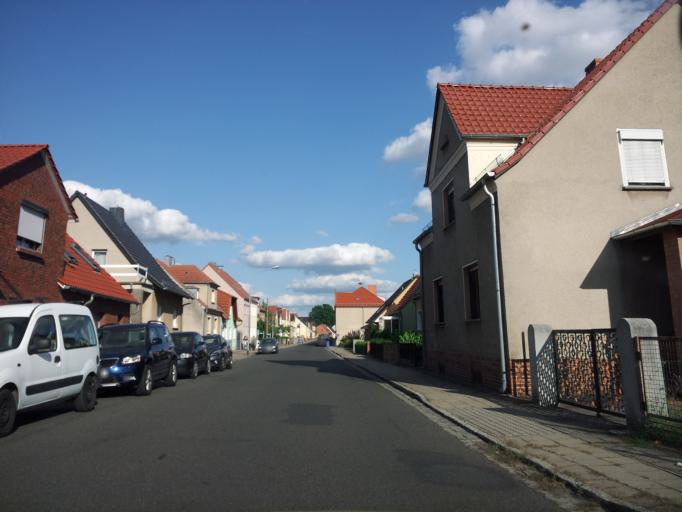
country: DE
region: Brandenburg
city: Juterbog
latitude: 51.9984
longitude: 13.0738
